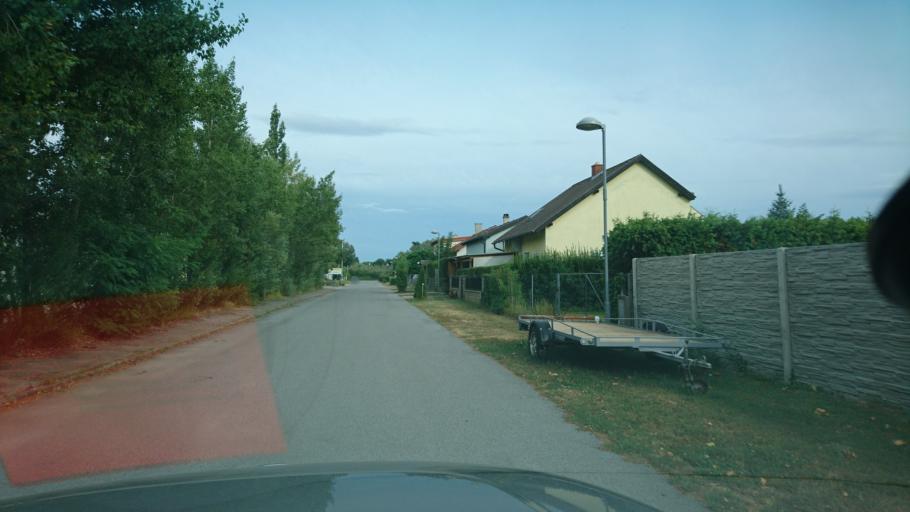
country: AT
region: Burgenland
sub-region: Politischer Bezirk Neusiedl am See
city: Neusiedl am See
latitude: 47.9378
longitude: 16.8459
